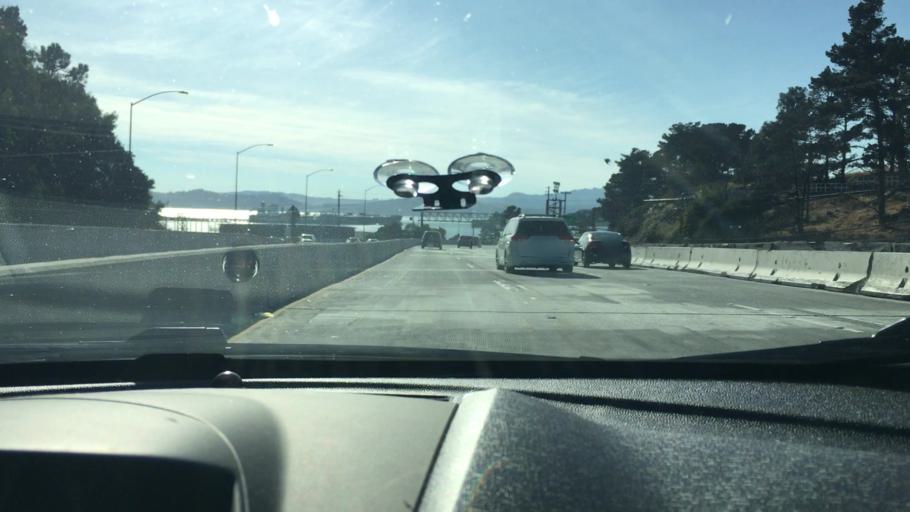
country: US
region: California
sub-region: Contra Costa County
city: North Richmond
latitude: 37.9325
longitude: -122.3978
